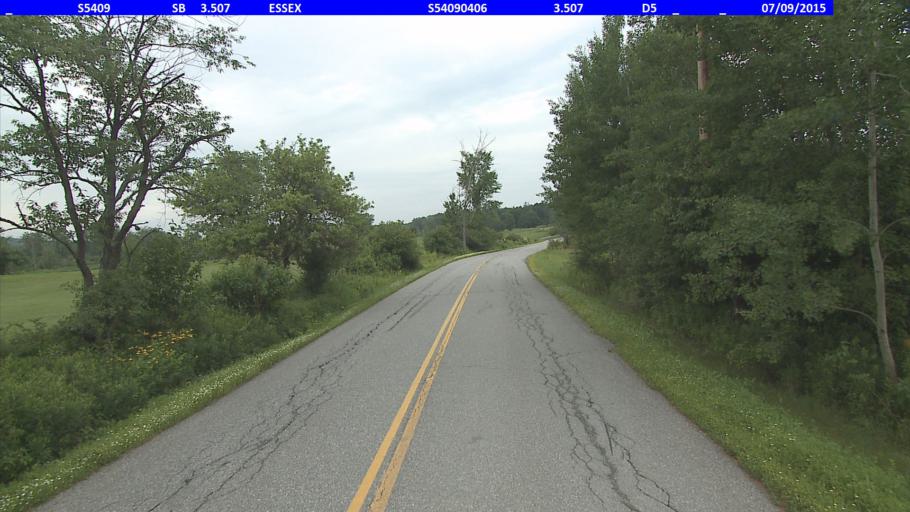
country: US
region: Vermont
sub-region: Chittenden County
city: Essex Junction
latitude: 44.5581
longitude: -73.0654
